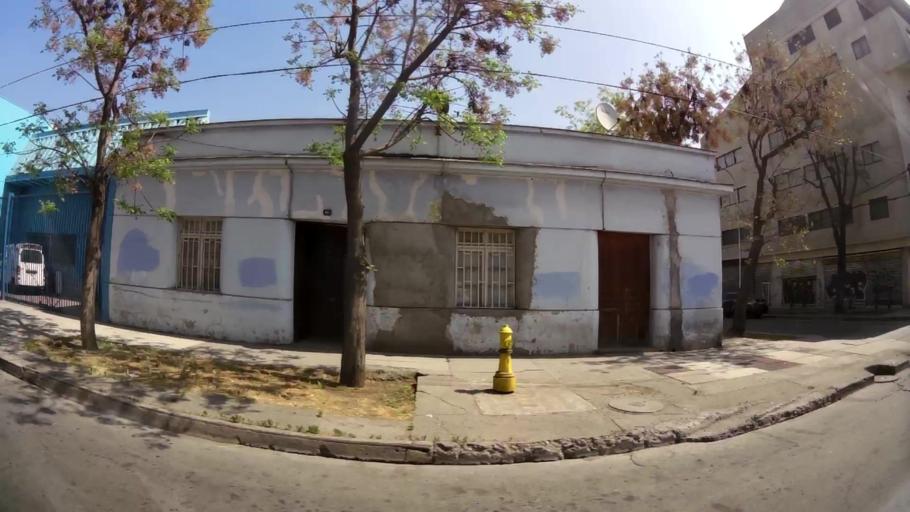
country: CL
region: Santiago Metropolitan
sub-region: Provincia de Santiago
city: Santiago
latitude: -33.4575
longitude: -70.6752
